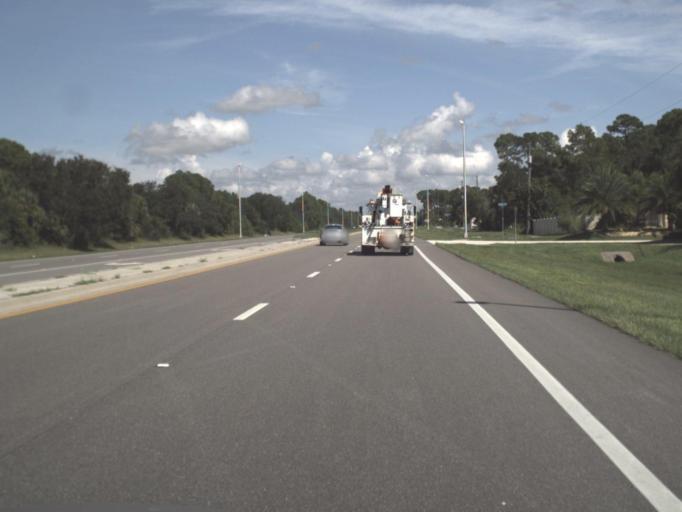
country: US
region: Florida
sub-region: Sarasota County
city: North Port
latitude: 27.0229
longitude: -82.1637
